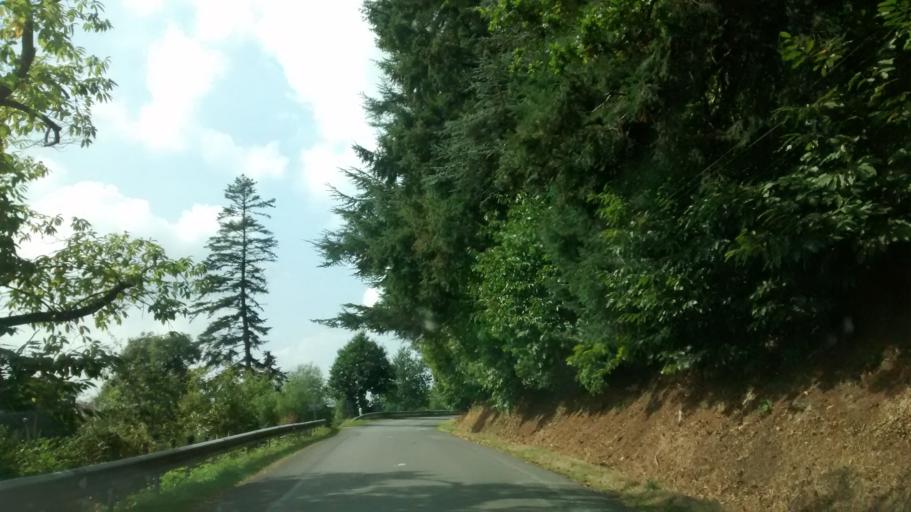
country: FR
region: Brittany
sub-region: Departement d'Ille-et-Vilaine
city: Chatillon-en-Vendelais
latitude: 48.2266
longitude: -1.1860
